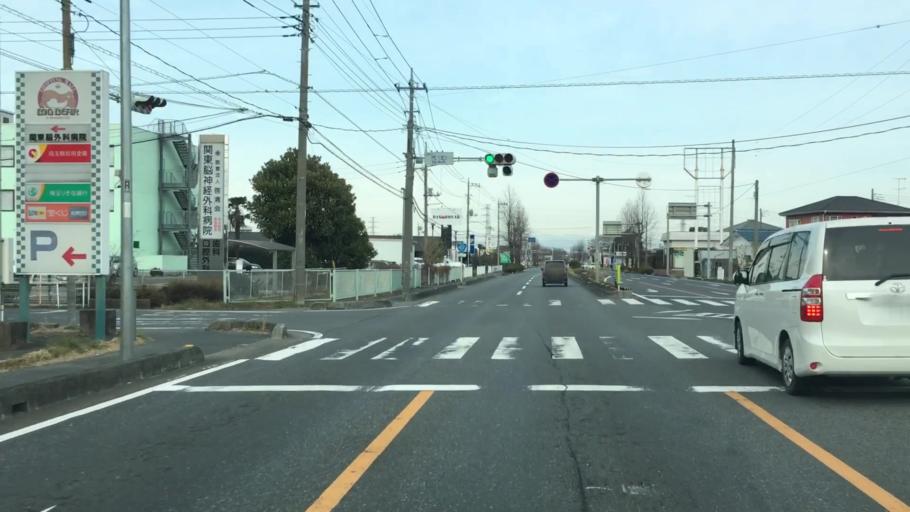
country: JP
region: Saitama
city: Kumagaya
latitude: 36.1746
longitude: 139.3701
